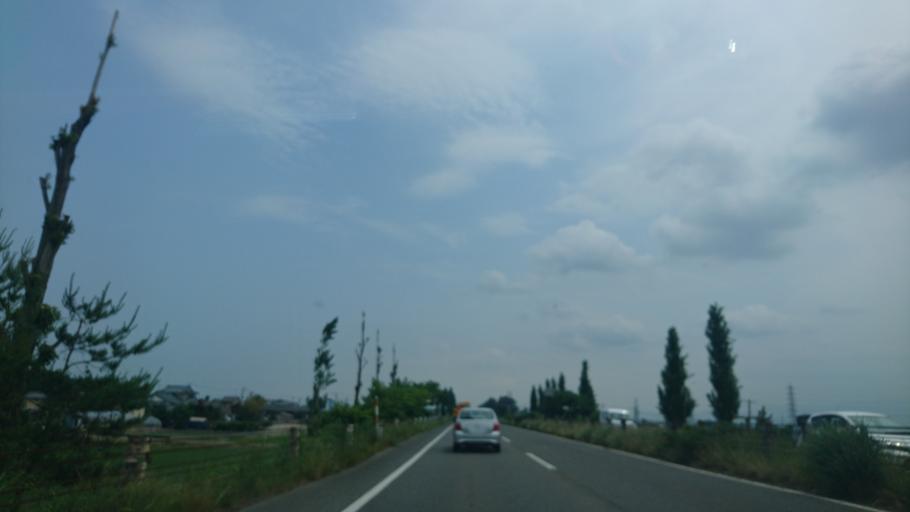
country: JP
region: Niigata
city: Kameda-honcho
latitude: 37.9362
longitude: 139.1691
